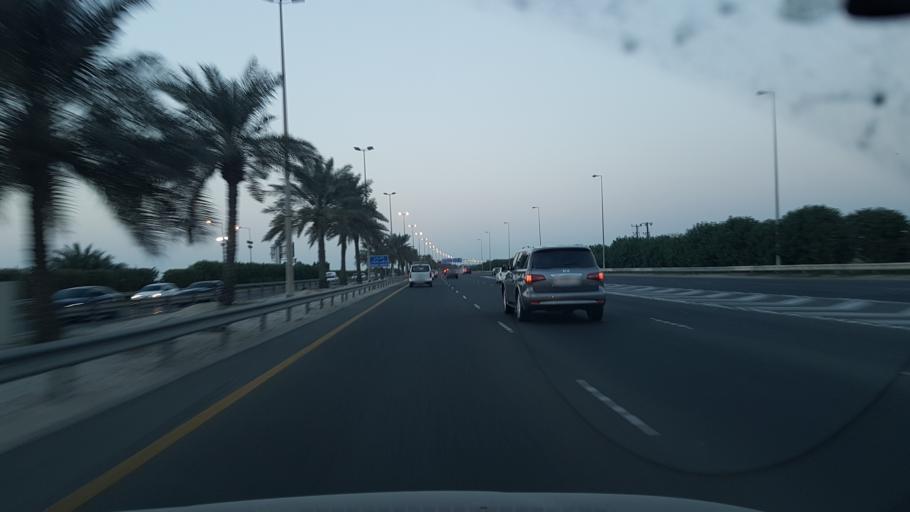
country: BH
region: Northern
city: Madinat `Isa
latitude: 26.1667
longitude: 50.5034
